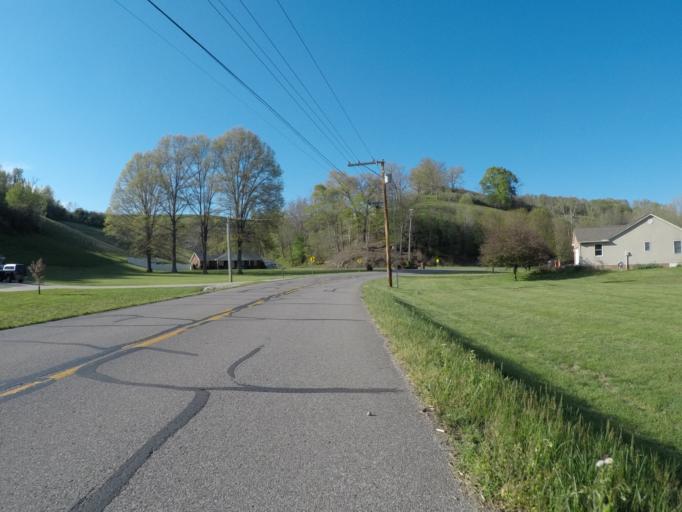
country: US
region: Kentucky
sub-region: Boyd County
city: Meads
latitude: 38.3634
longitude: -82.6887
